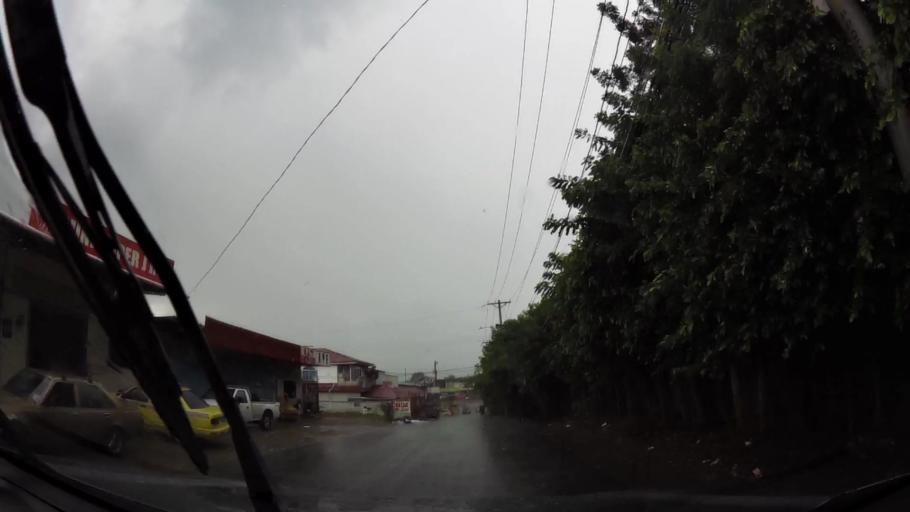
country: PA
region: Panama
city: Cabra Numero Uno
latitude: 9.1018
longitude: -79.3303
